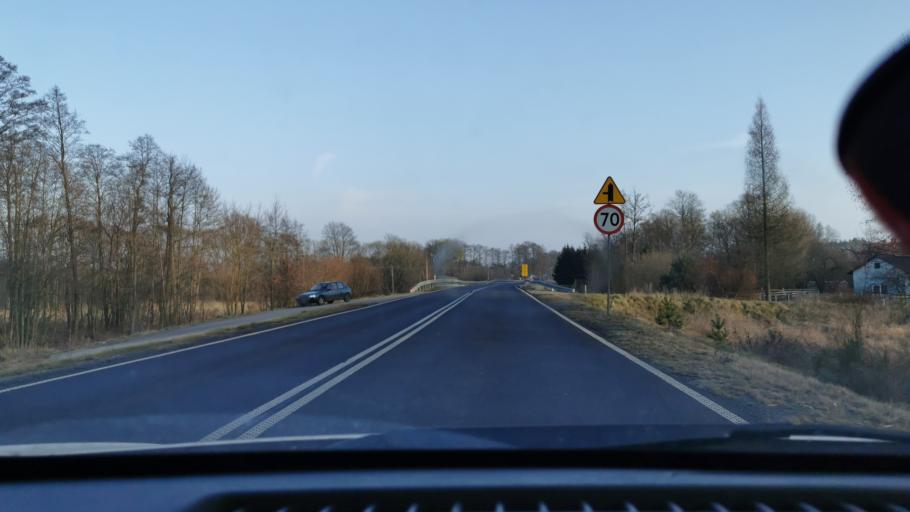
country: PL
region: Lodz Voivodeship
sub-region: Powiat pabianicki
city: Dlutow
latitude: 51.5262
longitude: 19.2985
